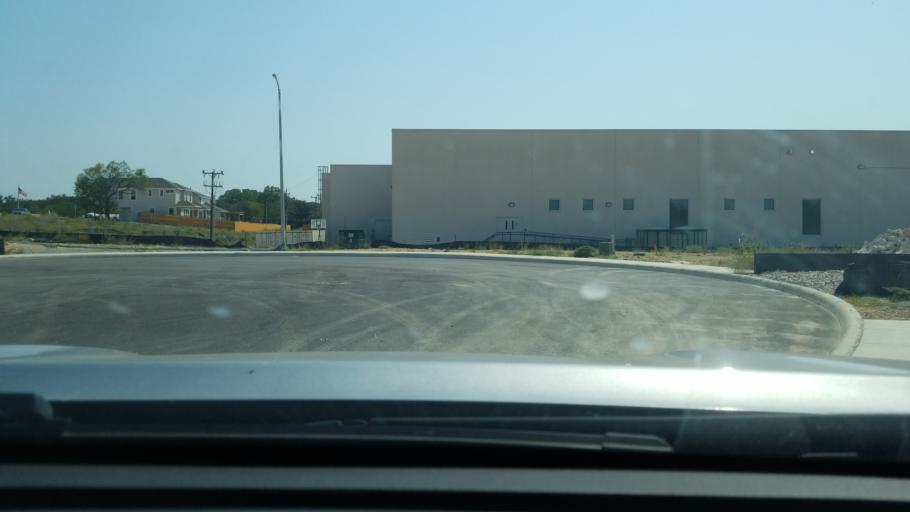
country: US
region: Texas
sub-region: Bexar County
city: Leon Valley
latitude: 29.5466
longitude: -98.6129
